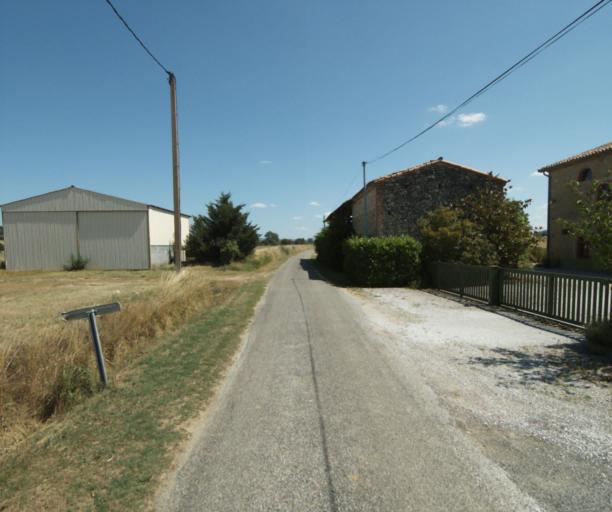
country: FR
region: Midi-Pyrenees
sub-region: Departement de la Haute-Garonne
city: Saint-Felix-Lauragais
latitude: 43.4893
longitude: 1.8755
